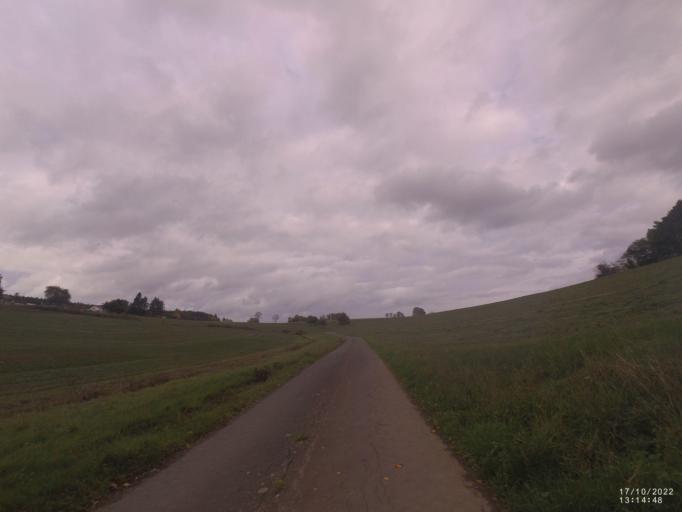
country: DE
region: Rheinland-Pfalz
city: Darscheid
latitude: 50.2170
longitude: 6.8783
